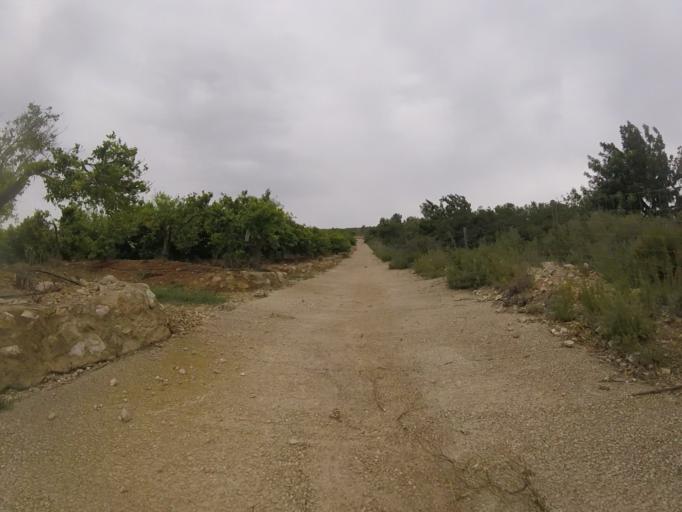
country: ES
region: Valencia
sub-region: Provincia de Castello
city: Alcala de Xivert
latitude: 40.2798
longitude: 0.2519
